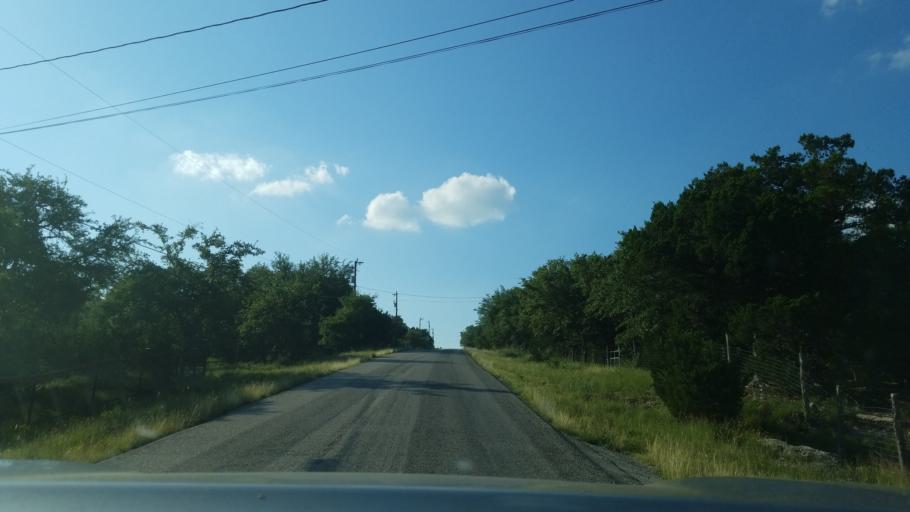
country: US
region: Texas
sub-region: Comal County
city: Bulverde
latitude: 29.7759
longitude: -98.4434
